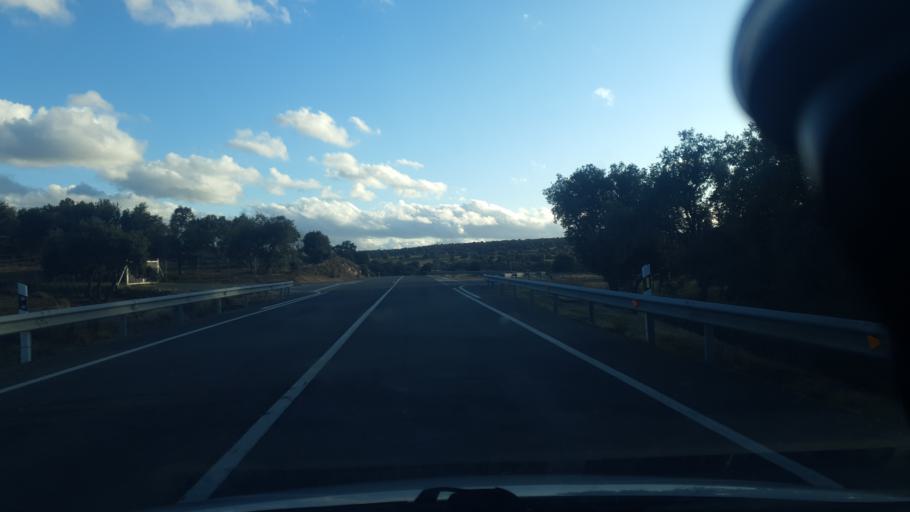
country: ES
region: Castille and Leon
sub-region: Provincia de Avila
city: Mingorria
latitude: 40.7353
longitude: -4.6750
